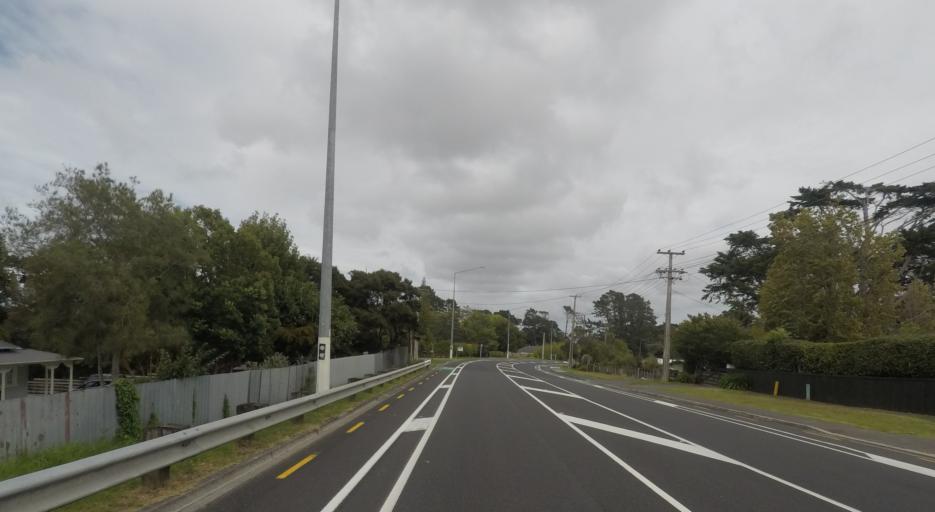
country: NZ
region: Auckland
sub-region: Auckland
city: North Shore
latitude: -36.7764
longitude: 174.6913
